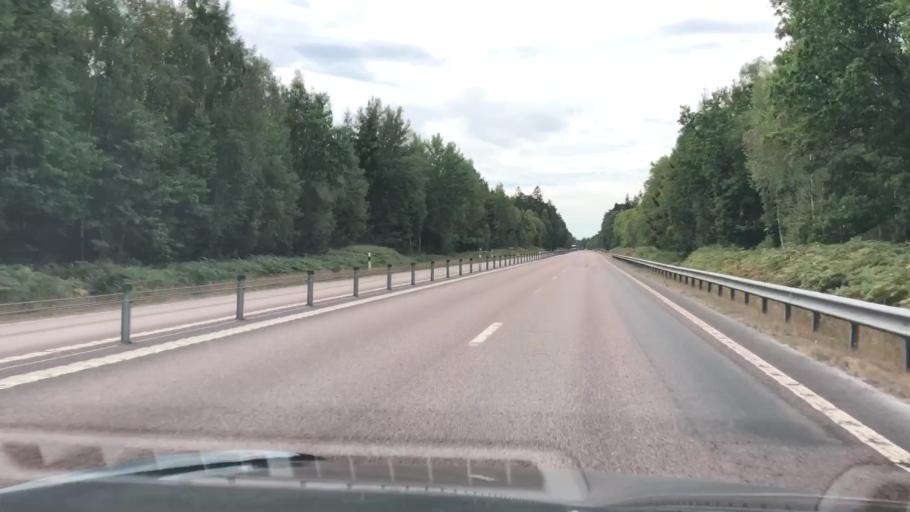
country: SE
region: Kalmar
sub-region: Torsas Kommun
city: Torsas
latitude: 56.2949
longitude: 15.9958
